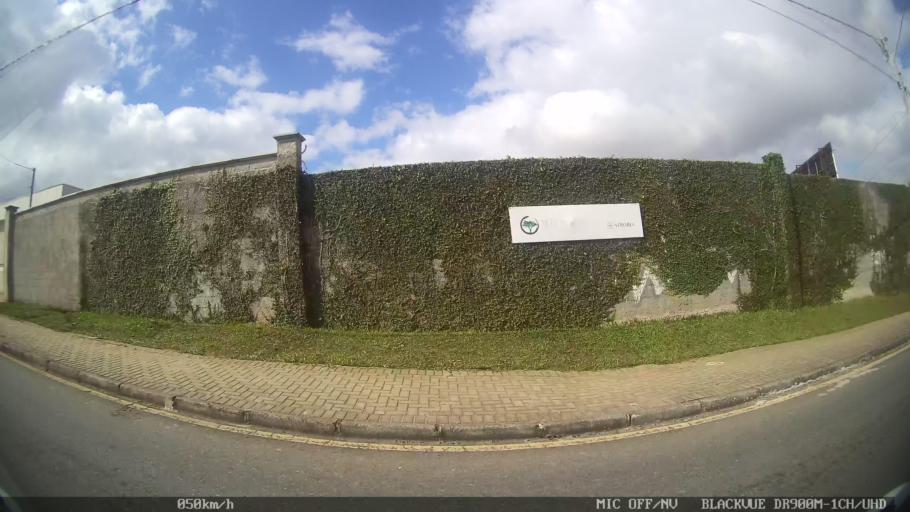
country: BR
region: Parana
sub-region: Pinhais
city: Pinhais
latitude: -25.3782
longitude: -49.2009
